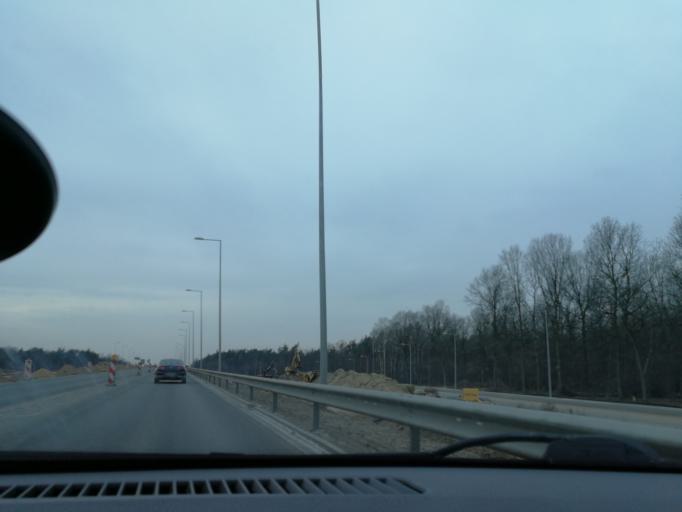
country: PL
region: Lublin Voivodeship
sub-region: Powiat pulawski
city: Pulawy
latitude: 51.4430
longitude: 21.9766
